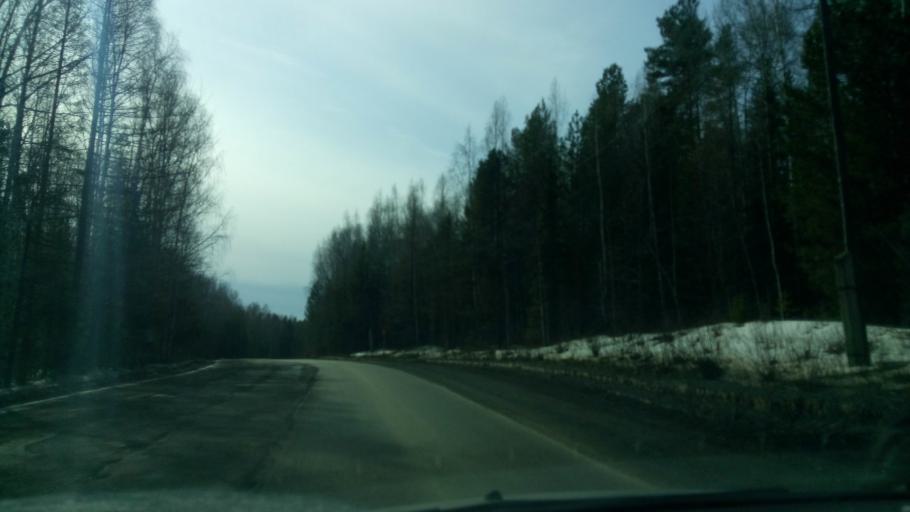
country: RU
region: Sverdlovsk
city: Chernoistochinsk
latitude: 57.7077
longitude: 59.7764
